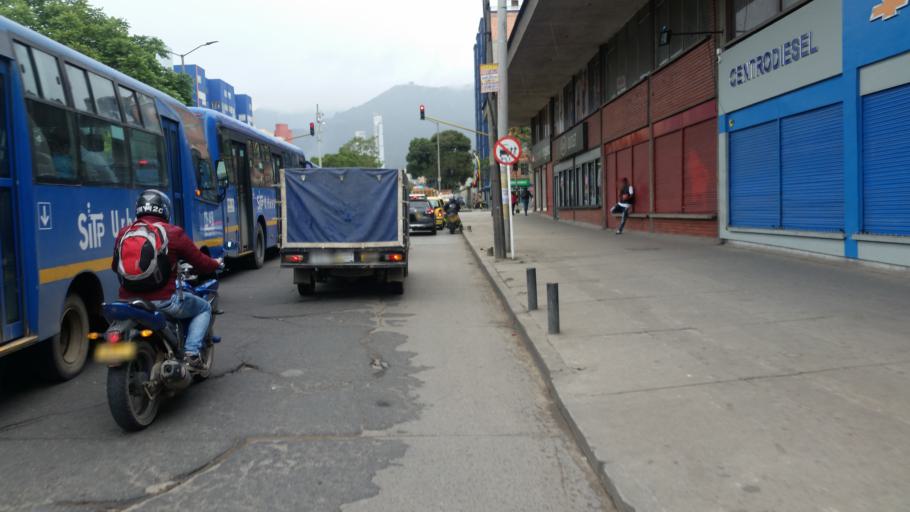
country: CO
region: Bogota D.C.
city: Bogota
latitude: 4.6147
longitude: -74.0843
